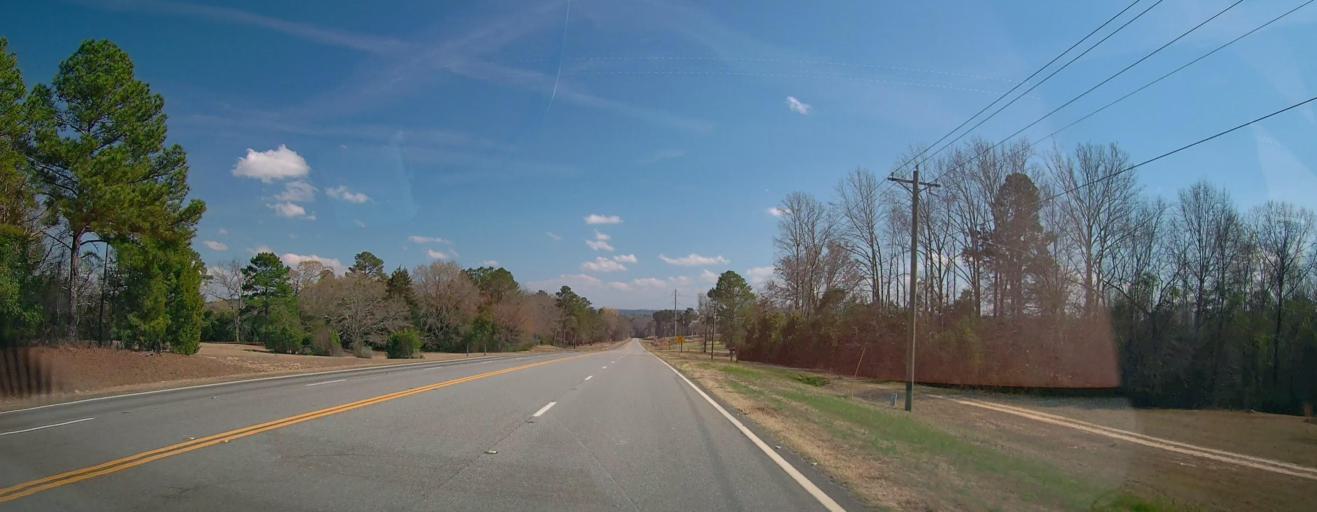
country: US
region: Georgia
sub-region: Wilkinson County
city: Gordon
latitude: 32.9093
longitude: -83.3805
